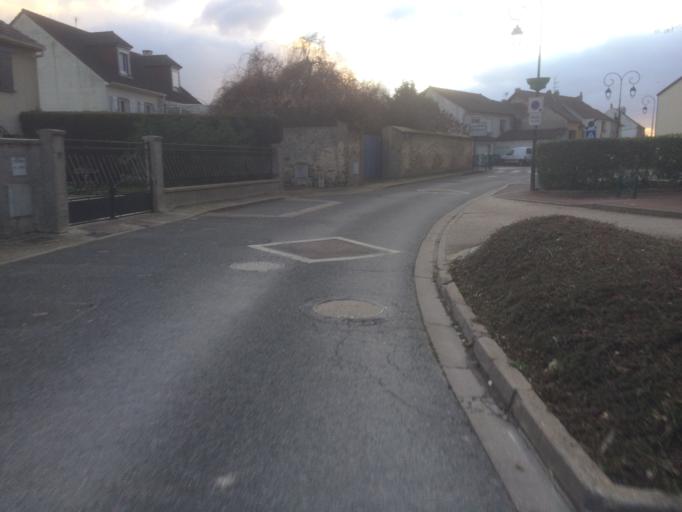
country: FR
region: Ile-de-France
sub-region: Departement de l'Essonne
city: Villejust
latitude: 48.6820
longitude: 2.2372
